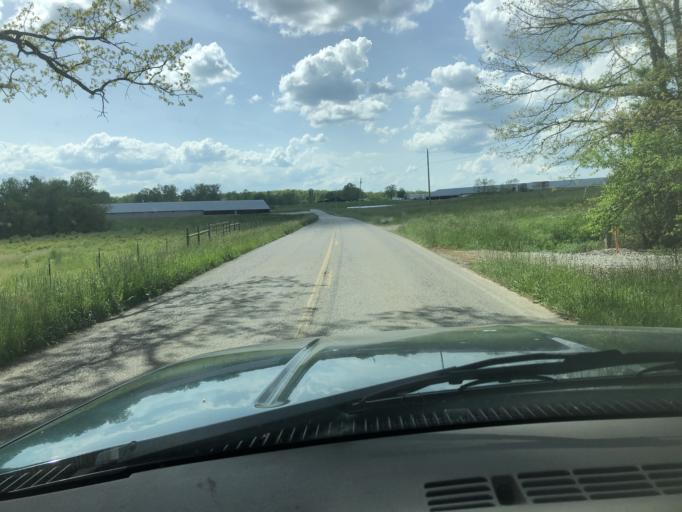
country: US
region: Tennessee
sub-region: Fentress County
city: Jamestown
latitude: 36.3148
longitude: -84.8578
